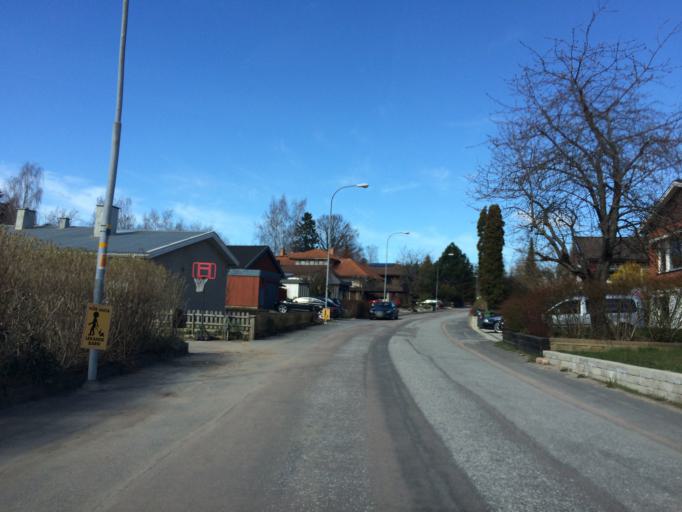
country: SE
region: Stockholm
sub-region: Sollentuna Kommun
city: Sollentuna
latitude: 59.4512
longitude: 17.9161
